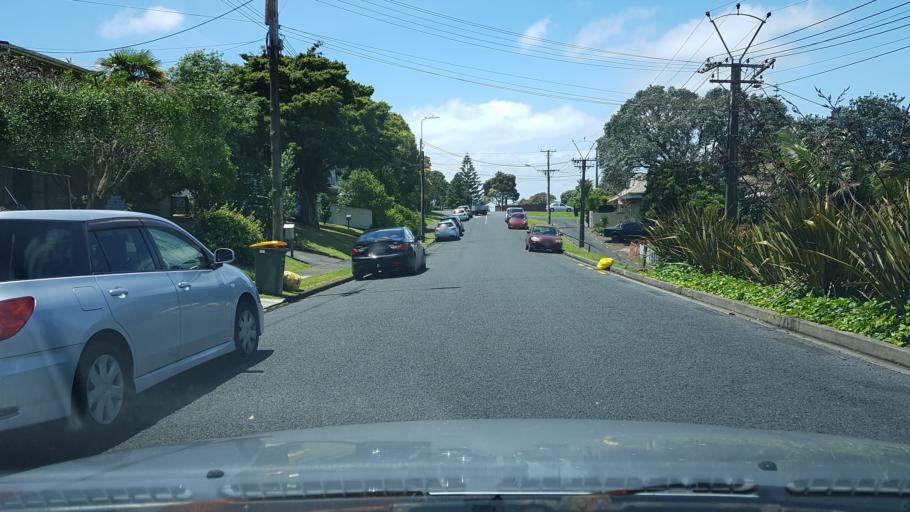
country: NZ
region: Auckland
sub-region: Auckland
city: North Shore
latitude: -36.8001
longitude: 174.7227
